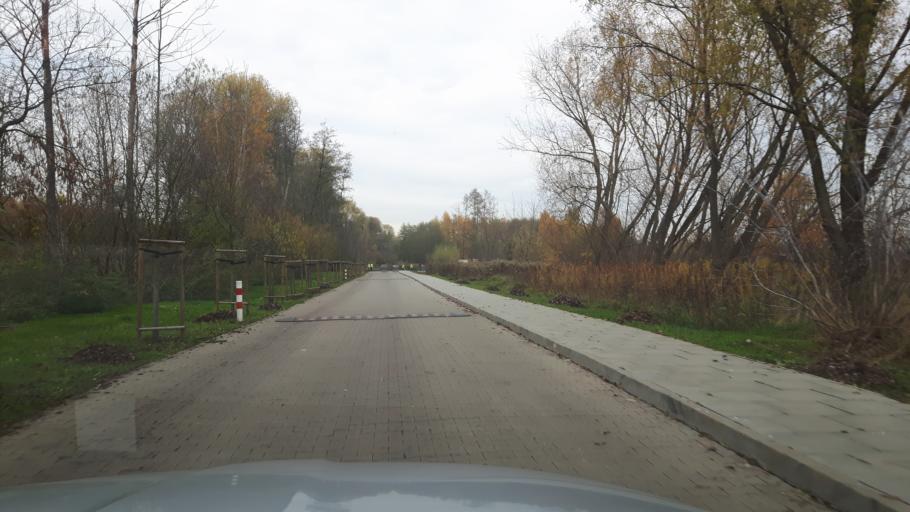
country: PL
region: Masovian Voivodeship
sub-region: Warszawa
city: Ursynow
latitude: 52.1574
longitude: 21.0619
